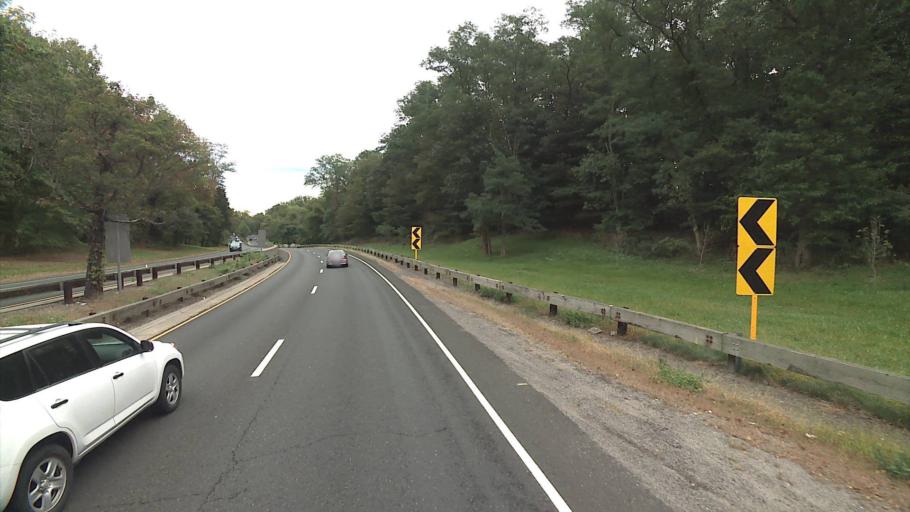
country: US
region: Connecticut
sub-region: Fairfield County
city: Cos Cob
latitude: 41.0896
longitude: -73.6243
